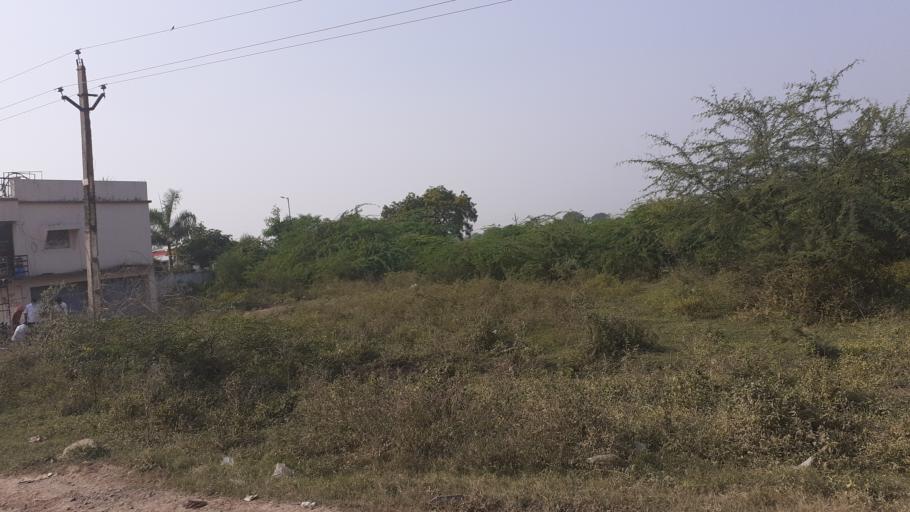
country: IN
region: Maharashtra
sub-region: Chandrapur
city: Warora
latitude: 20.3286
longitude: 79.1415
